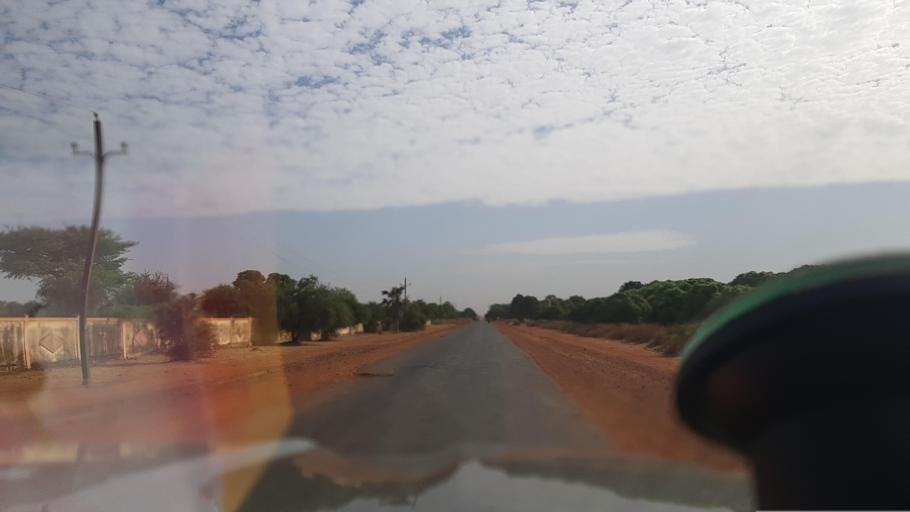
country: ML
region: Segou
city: Segou
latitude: 13.4986
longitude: -6.1572
